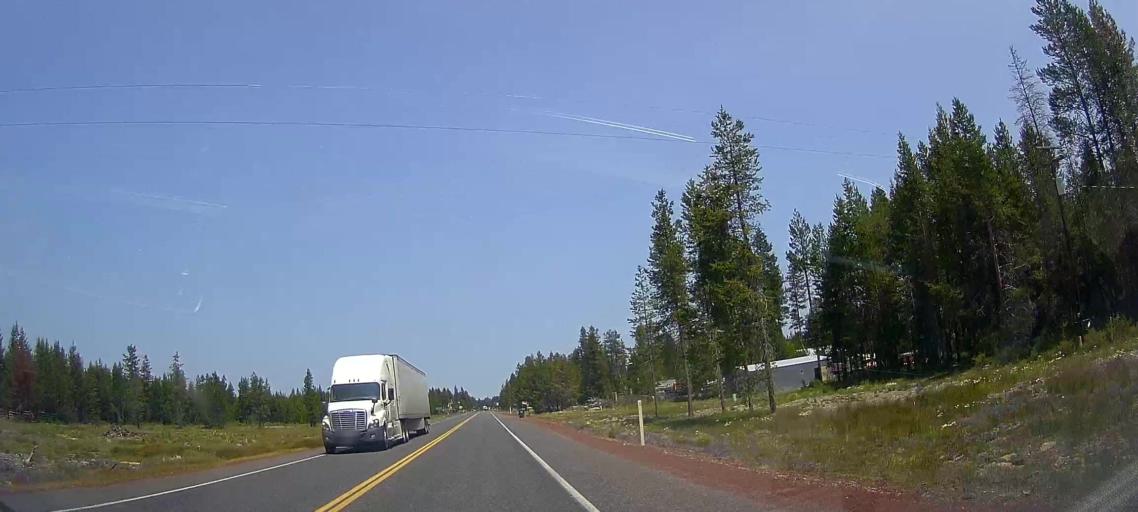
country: US
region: Oregon
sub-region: Deschutes County
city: La Pine
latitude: 43.4499
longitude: -121.7050
